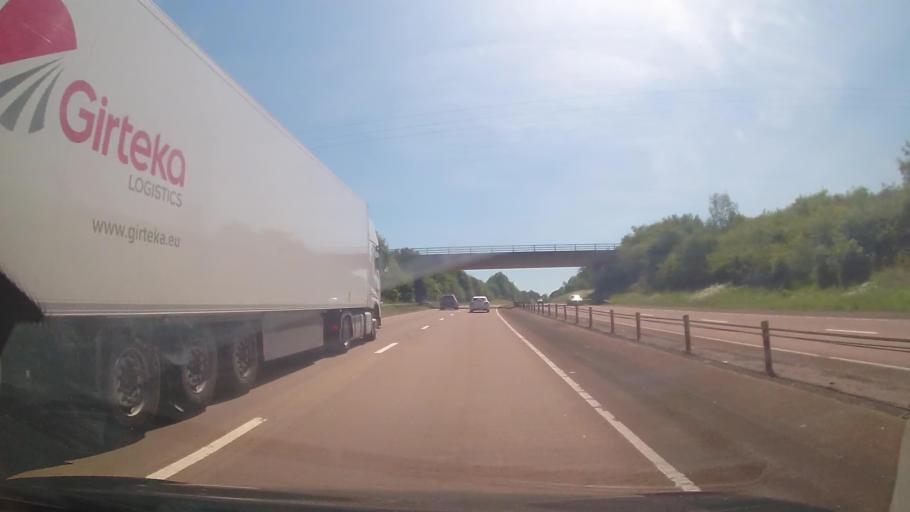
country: GB
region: England
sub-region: Devon
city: Newton Poppleford
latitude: 50.7390
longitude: -3.3654
